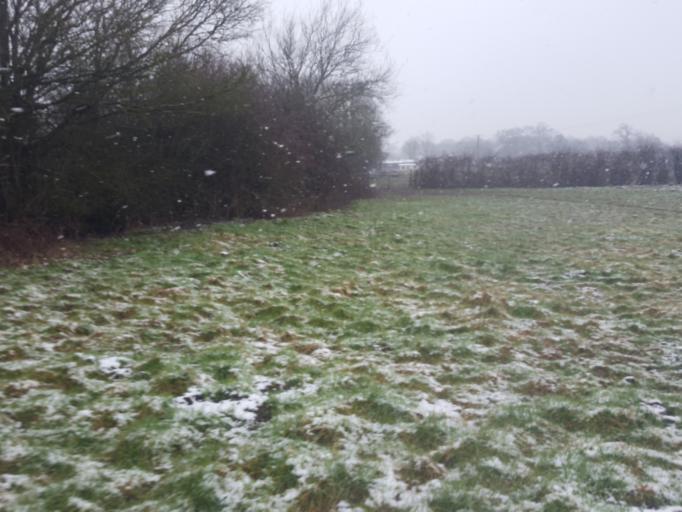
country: GB
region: England
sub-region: West Sussex
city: Gossops Green
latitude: 51.1248
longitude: -0.2351
